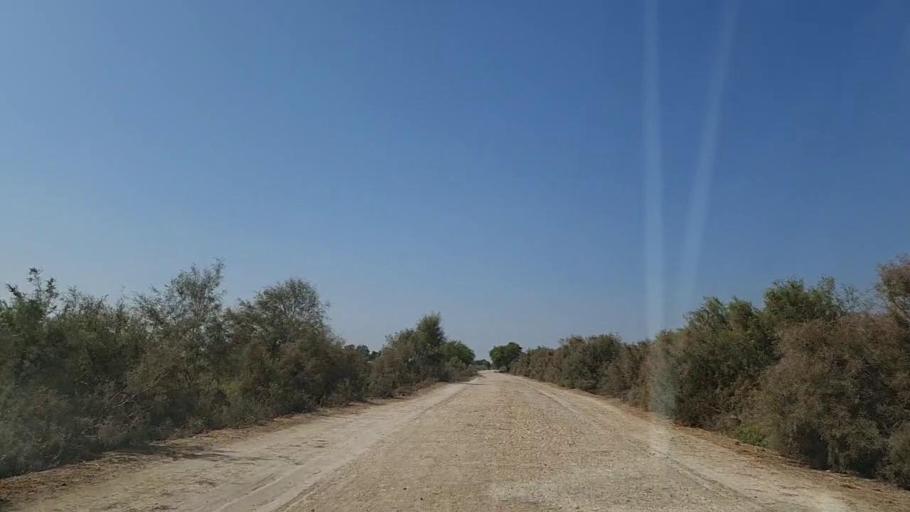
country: PK
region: Sindh
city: Chuhar Jamali
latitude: 24.4186
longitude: 68.0208
